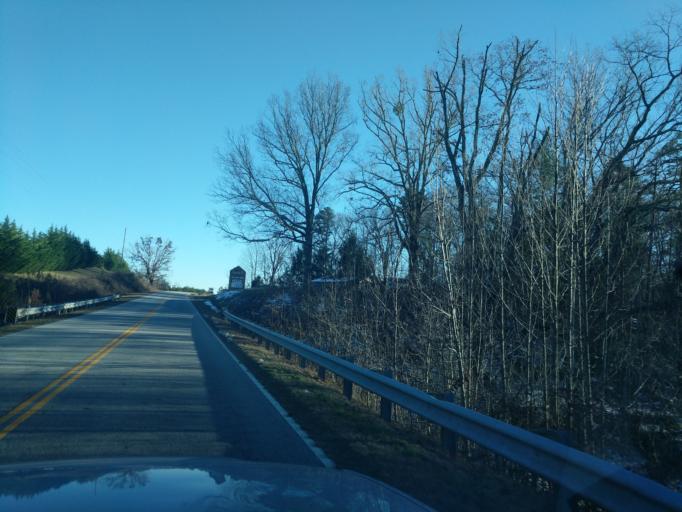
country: US
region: Georgia
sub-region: Rabun County
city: Clayton
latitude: 34.7995
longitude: -83.2725
